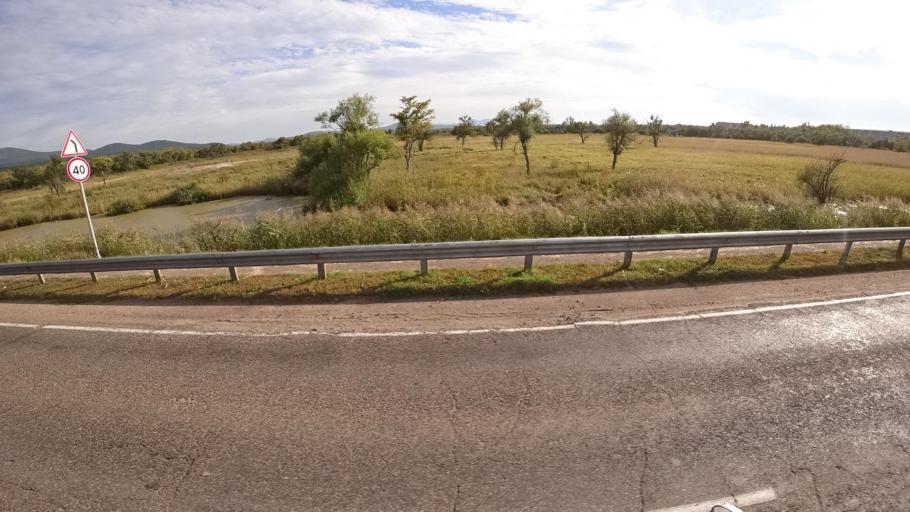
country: RU
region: Primorskiy
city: Dostoyevka
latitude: 44.2939
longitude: 133.4338
